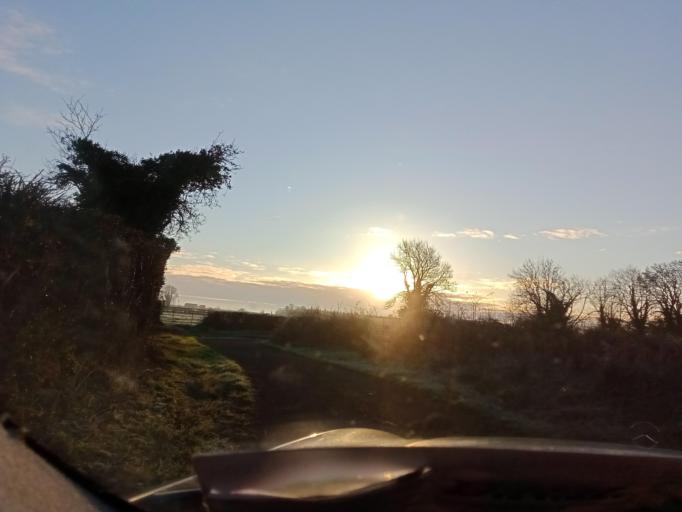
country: IE
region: Leinster
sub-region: Kilkenny
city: Callan
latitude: 52.5420
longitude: -7.4243
